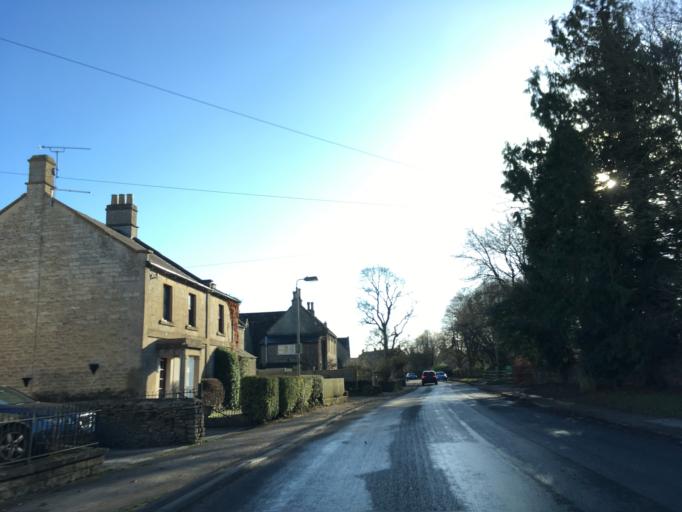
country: GB
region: England
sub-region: Wiltshire
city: Biddestone
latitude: 51.4849
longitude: -2.1920
